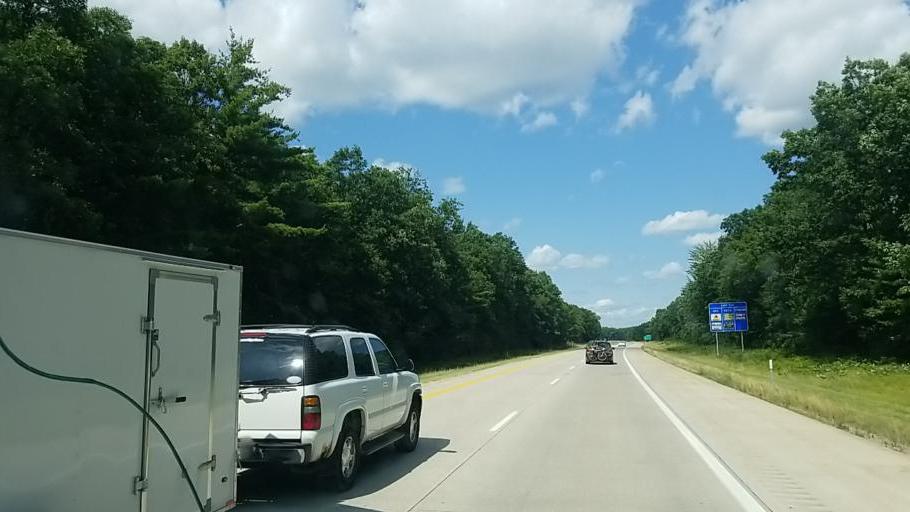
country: US
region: Michigan
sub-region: Montcalm County
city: Howard City
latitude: 43.4135
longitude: -85.5043
